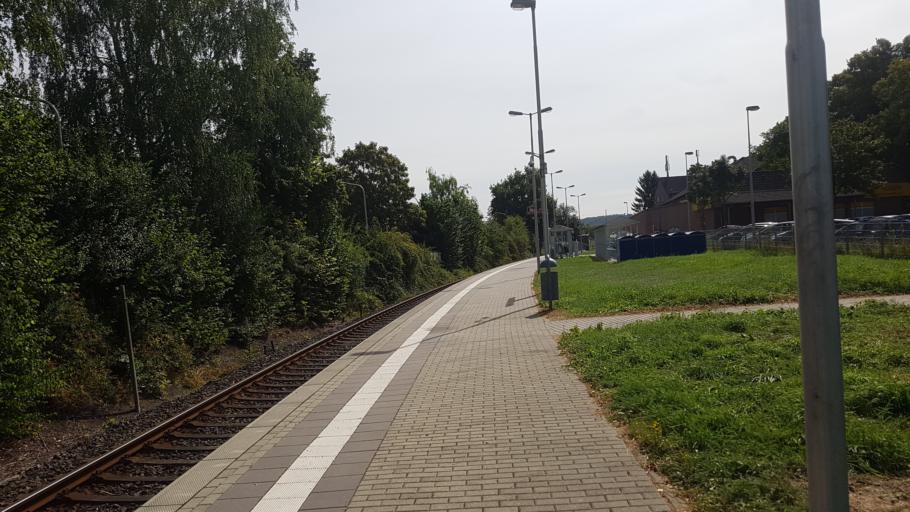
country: DE
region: North Rhine-Westphalia
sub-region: Regierungsbezirk Koln
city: Herzogenrath
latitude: 50.8876
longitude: 6.1186
